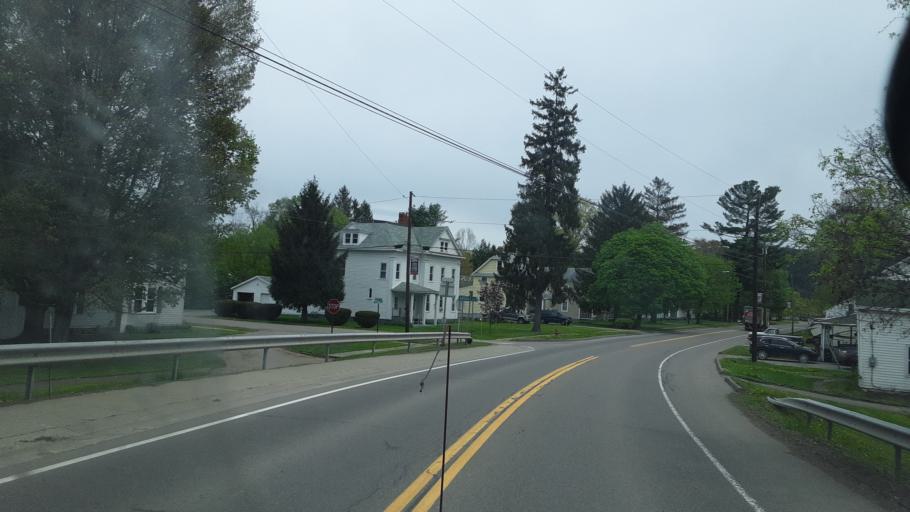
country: US
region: New York
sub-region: Steuben County
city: Addison
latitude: 42.1027
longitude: -77.2413
